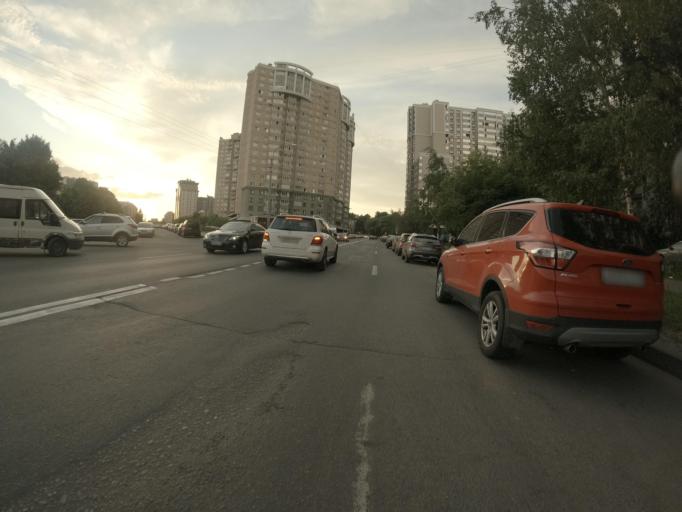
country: RU
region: St.-Petersburg
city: Kupchino
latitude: 59.8393
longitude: 30.3109
